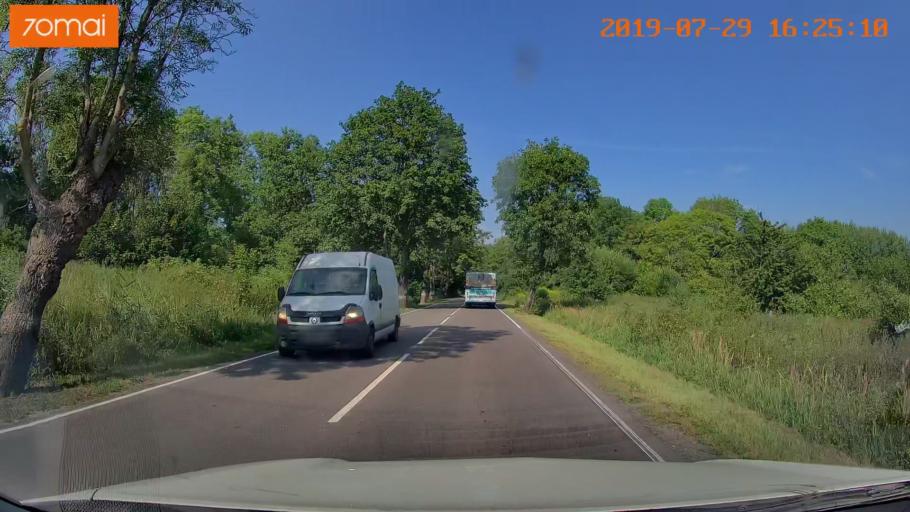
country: RU
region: Kaliningrad
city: Primorsk
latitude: 54.7209
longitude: 19.9639
